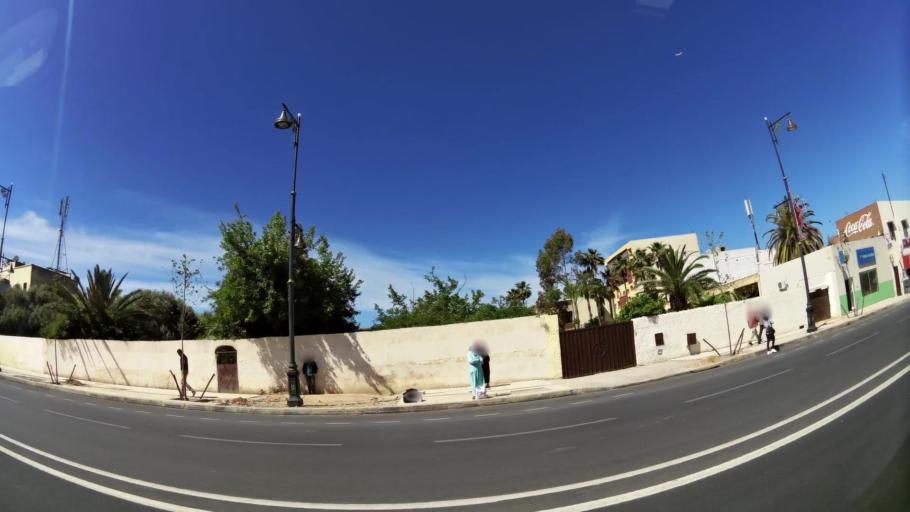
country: MA
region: Meknes-Tafilalet
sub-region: Meknes
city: Meknes
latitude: 33.8672
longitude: -5.5374
